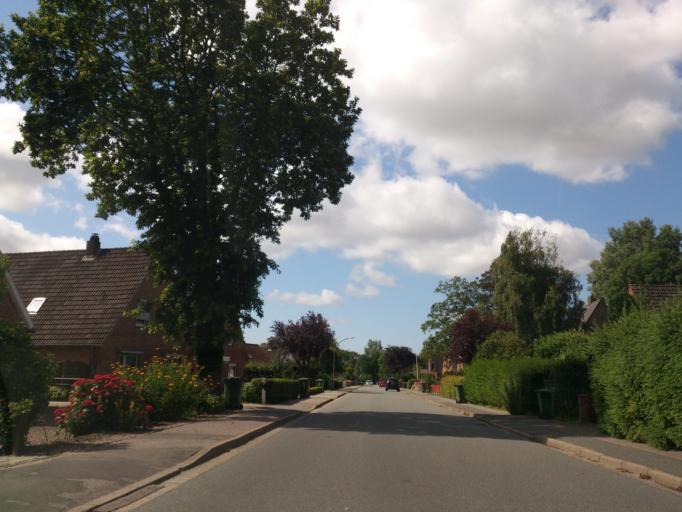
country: DE
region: Schleswig-Holstein
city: Tonning
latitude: 54.3048
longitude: 8.9274
